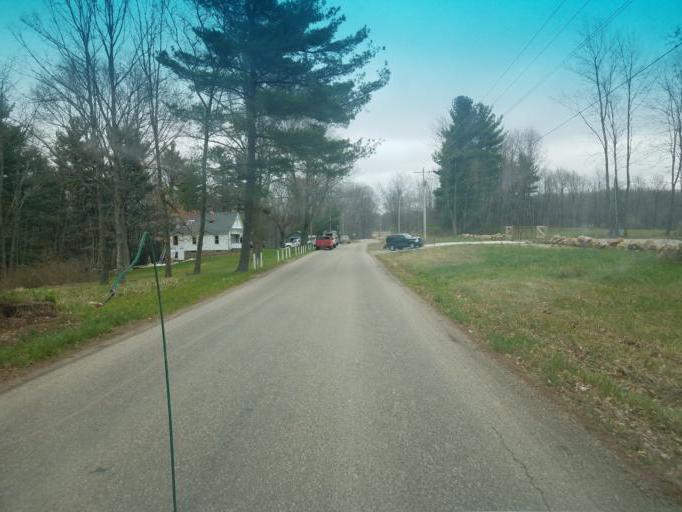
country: US
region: Ohio
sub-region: Stark County
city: Beach City
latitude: 40.6300
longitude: -81.6504
